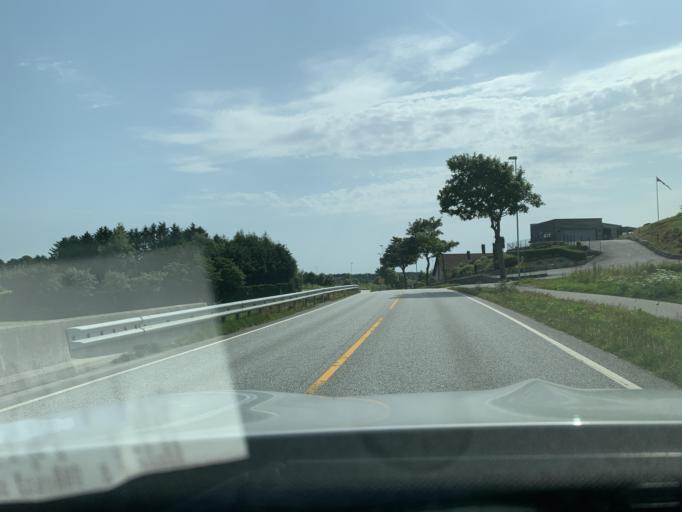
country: NO
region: Rogaland
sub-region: Klepp
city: Kleppe
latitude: 58.7621
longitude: 5.6238
